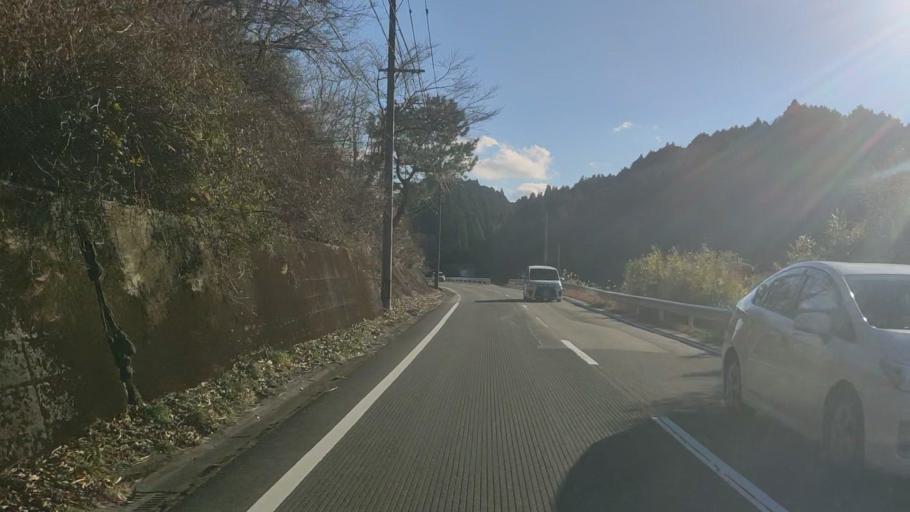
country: JP
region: Saga Prefecture
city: Kanzakimachi-kanzaki
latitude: 33.4082
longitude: 130.2722
